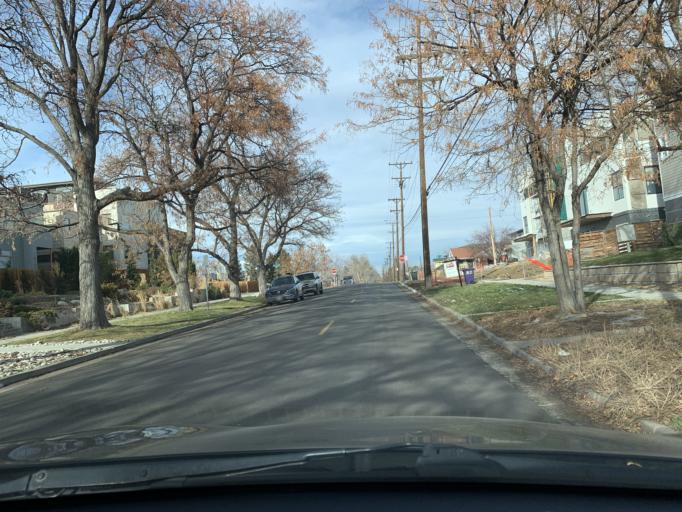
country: US
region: Colorado
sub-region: Jefferson County
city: Edgewater
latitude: 39.7457
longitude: -105.0298
